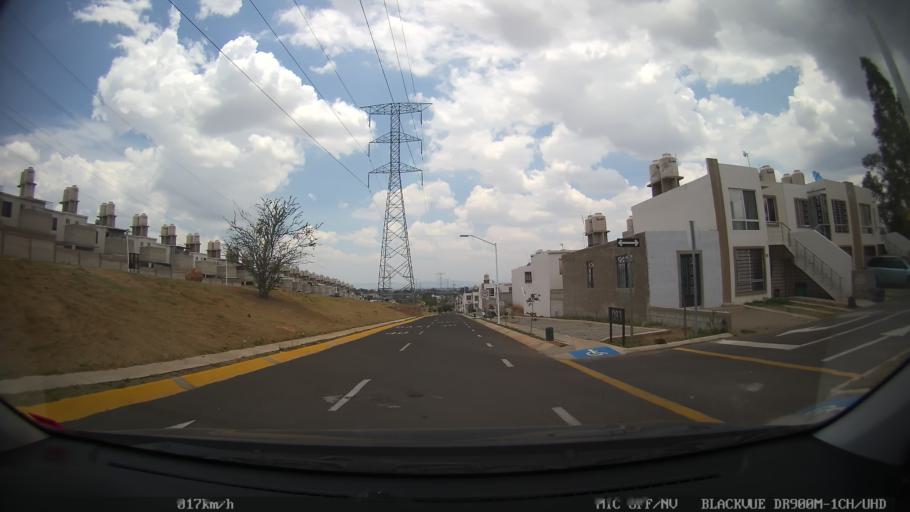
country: MX
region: Jalisco
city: Tonala
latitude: 20.6442
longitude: -103.2238
